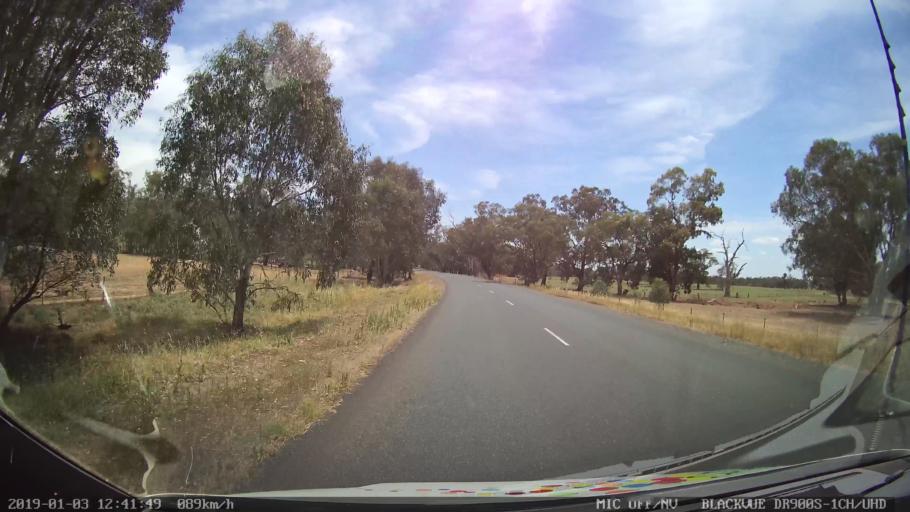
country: AU
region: New South Wales
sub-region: Weddin
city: Grenfell
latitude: -33.7946
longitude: 148.2153
